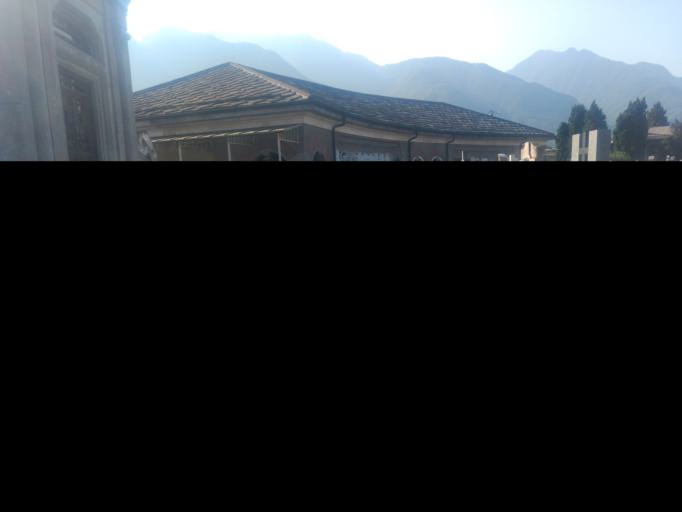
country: IT
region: Piedmont
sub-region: Provincia Verbano-Cusio-Ossola
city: Domodossola
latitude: 46.1088
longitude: 8.2985
